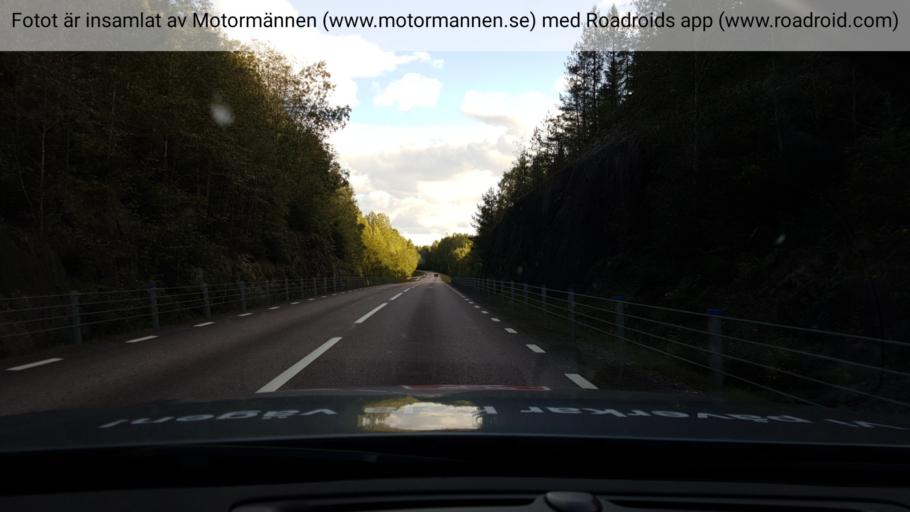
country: SE
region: Vaermland
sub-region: Karlstads Kommun
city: Molkom
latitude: 59.6545
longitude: 13.7108
